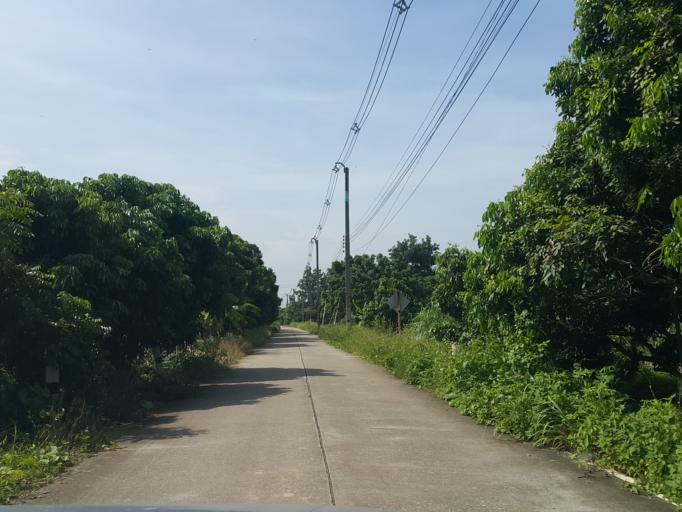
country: TH
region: Chiang Mai
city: Saraphi
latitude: 18.6869
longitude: 99.0689
